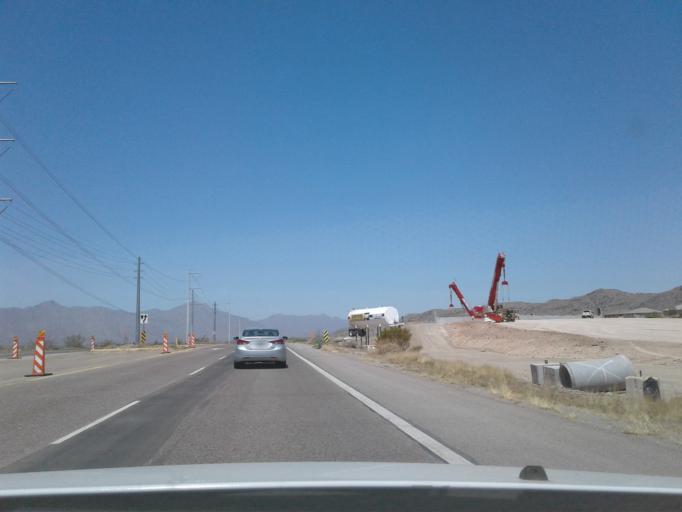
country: US
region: Arizona
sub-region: Maricopa County
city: Laveen
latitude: 33.2910
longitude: -112.0950
